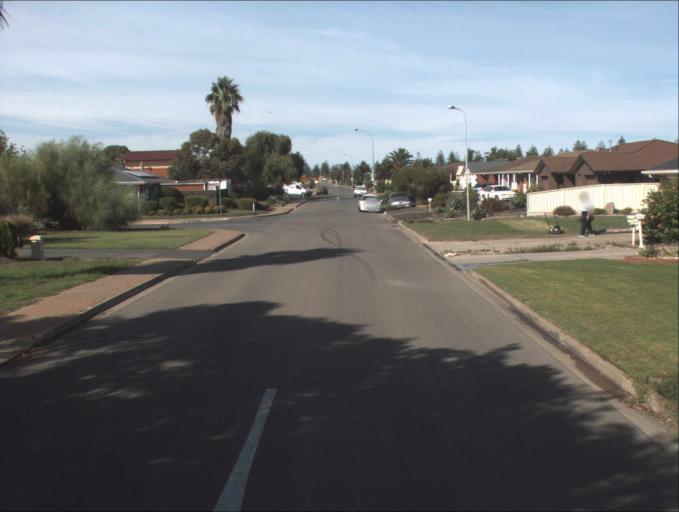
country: AU
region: South Australia
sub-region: Port Adelaide Enfield
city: Birkenhead
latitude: -34.7815
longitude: 138.4936
